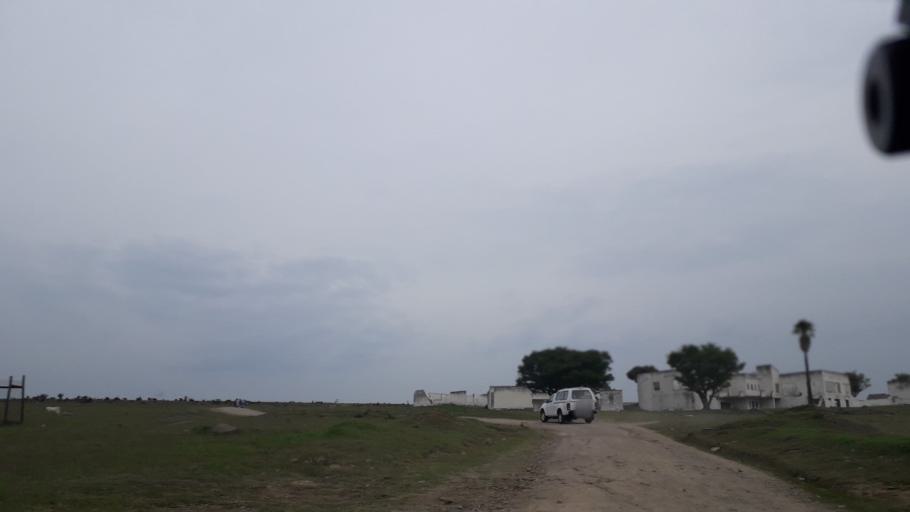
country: ZA
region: Eastern Cape
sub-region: Buffalo City Metropolitan Municipality
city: Bhisho
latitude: -32.8313
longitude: 27.3760
